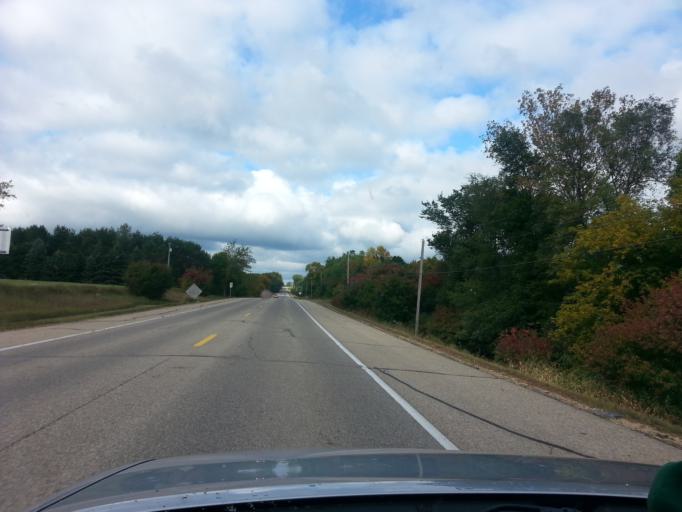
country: US
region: Minnesota
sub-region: Washington County
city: Lake Elmo
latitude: 44.9636
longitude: -92.8859
